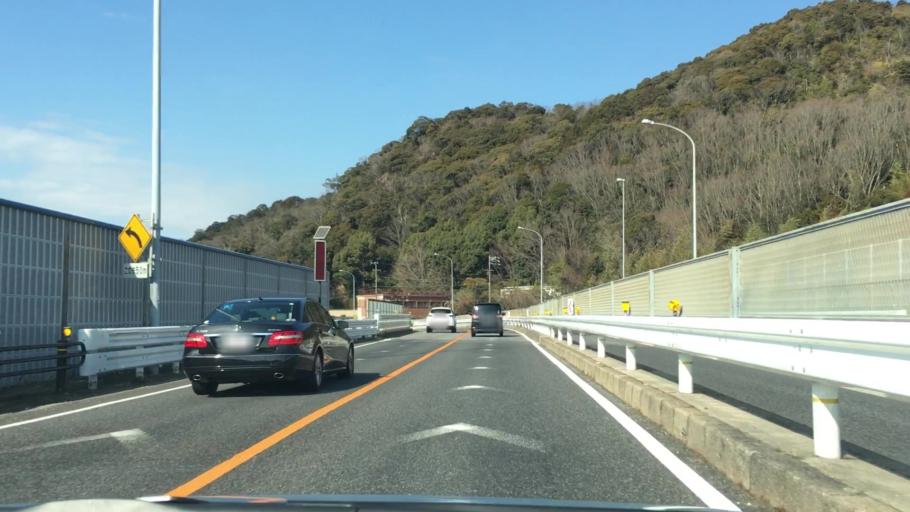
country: JP
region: Aichi
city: Okazaki
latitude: 34.9091
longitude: 137.2294
